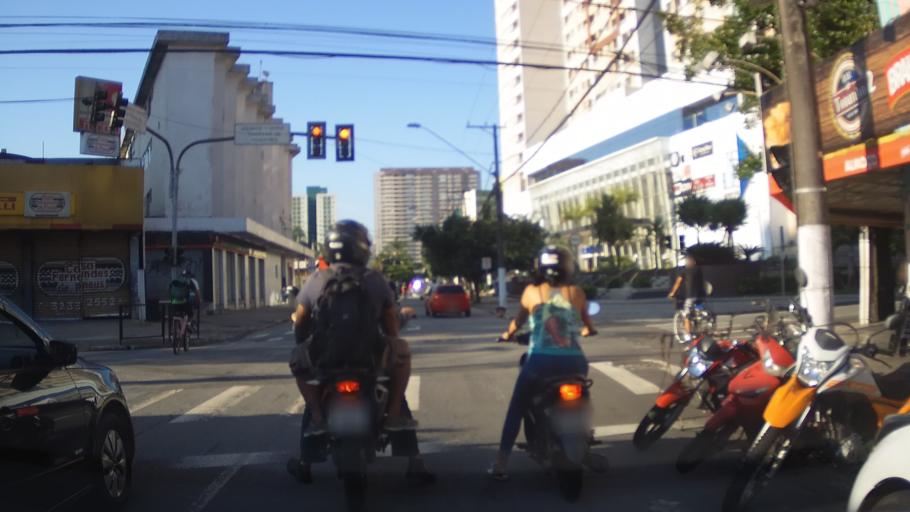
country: BR
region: Sao Paulo
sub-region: Santos
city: Santos
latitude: -23.9513
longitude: -46.3273
